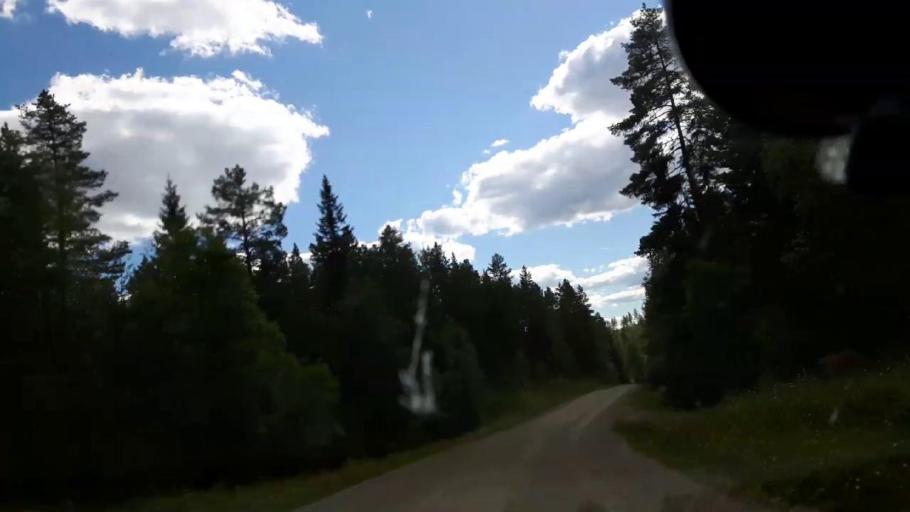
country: SE
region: Vaesternorrland
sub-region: Ange Kommun
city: Ange
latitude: 62.7287
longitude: 15.6430
